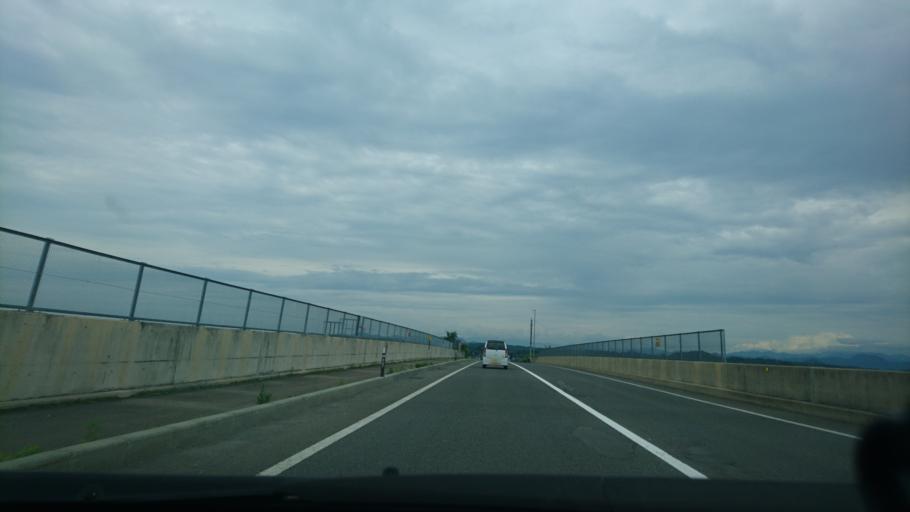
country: JP
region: Akita
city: Omagari
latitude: 39.4909
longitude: 140.4514
